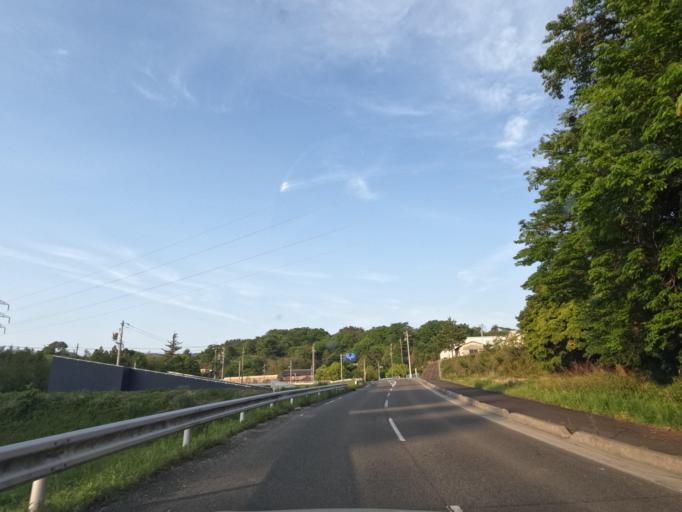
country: JP
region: Mie
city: Komono
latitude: 35.1468
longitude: 136.5261
